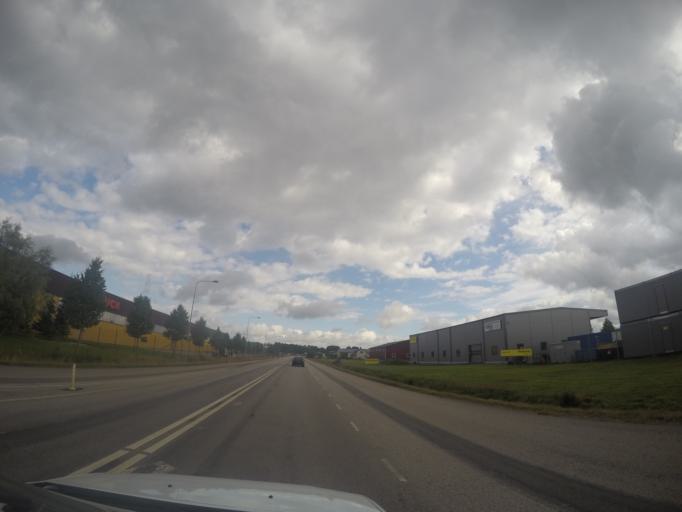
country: SE
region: Kronoberg
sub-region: Ljungby Kommun
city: Ljungby
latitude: 56.8147
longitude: 13.9169
